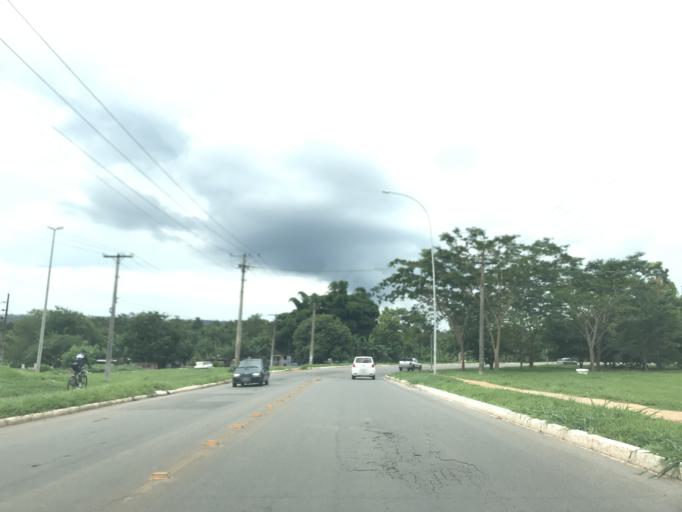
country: BR
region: Federal District
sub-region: Brasilia
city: Brasilia
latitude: -15.6548
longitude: -47.8132
